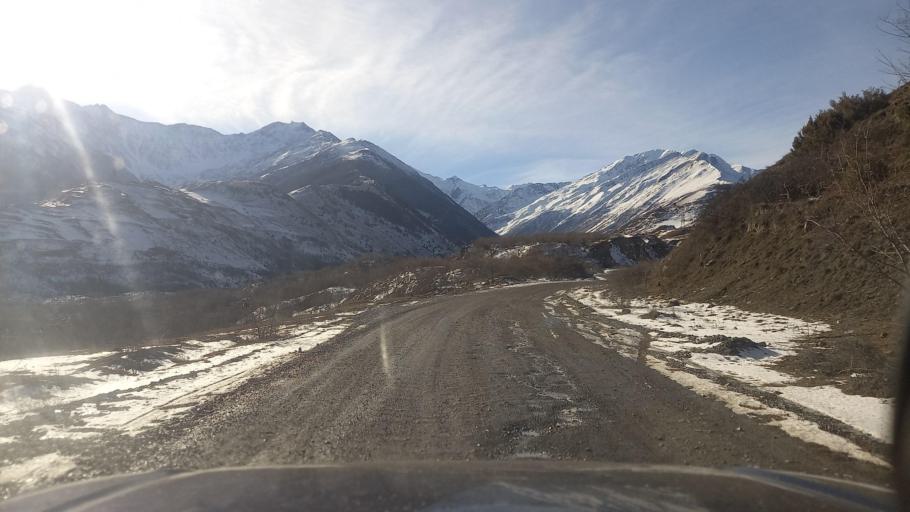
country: RU
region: Ingushetiya
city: Dzhayrakh
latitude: 42.8508
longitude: 44.5193
